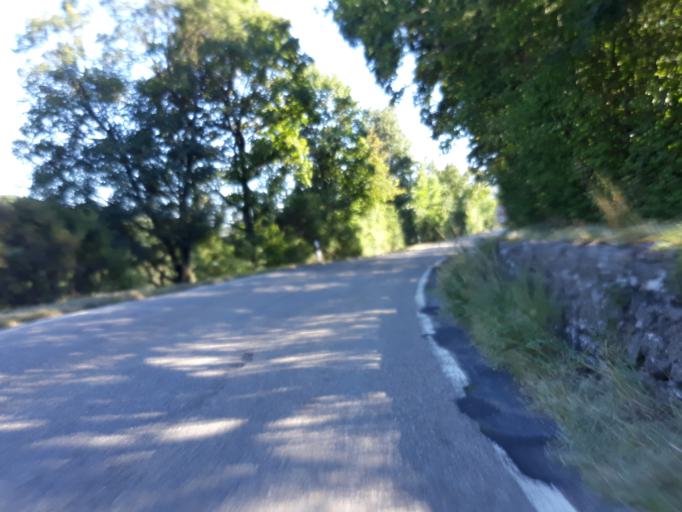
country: DE
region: Baden-Wuerttemberg
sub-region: Regierungsbezirk Stuttgart
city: Aidlingen
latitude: 48.6908
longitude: 8.8995
